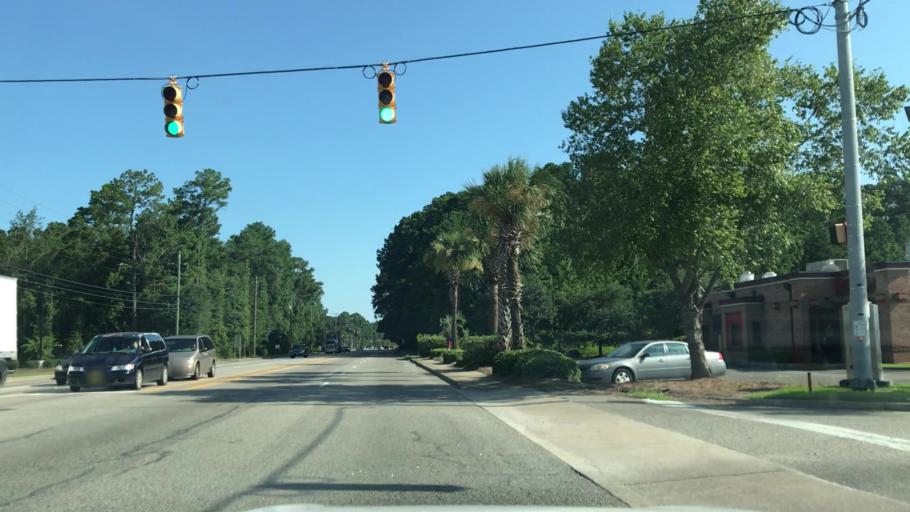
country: US
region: South Carolina
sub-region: Georgetown County
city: Georgetown
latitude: 33.3945
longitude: -79.2891
